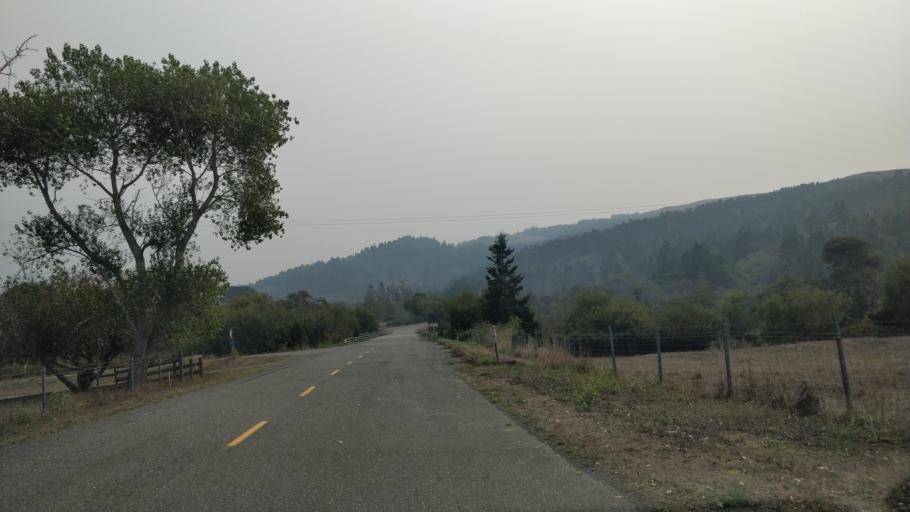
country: US
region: California
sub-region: Humboldt County
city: Ferndale
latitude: 40.4667
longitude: -124.3684
